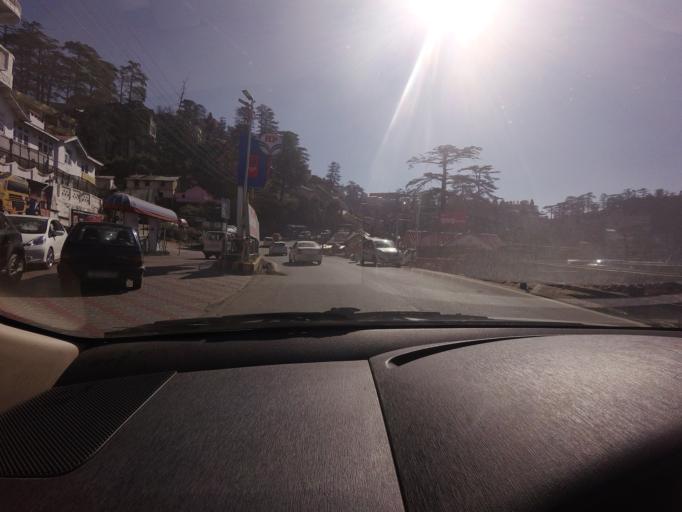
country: IN
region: Himachal Pradesh
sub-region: Shimla
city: Shimla
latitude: 31.1083
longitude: 77.1650
